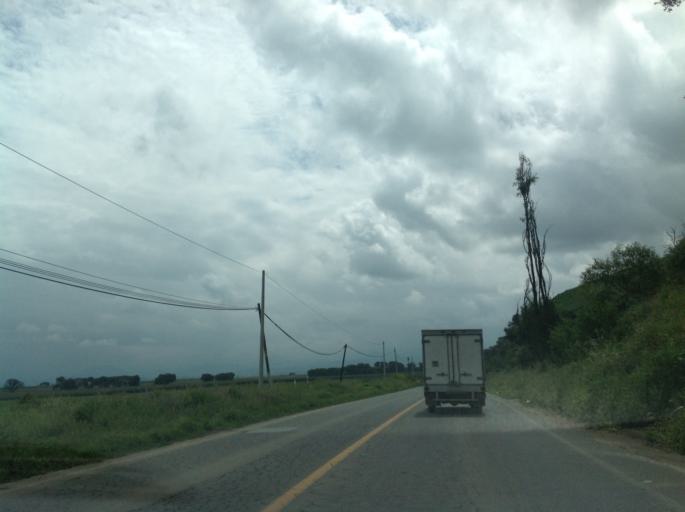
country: MX
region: Mexico
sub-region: Rayon
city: Colonia Emiliano Zapata
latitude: 19.1166
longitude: -99.5590
